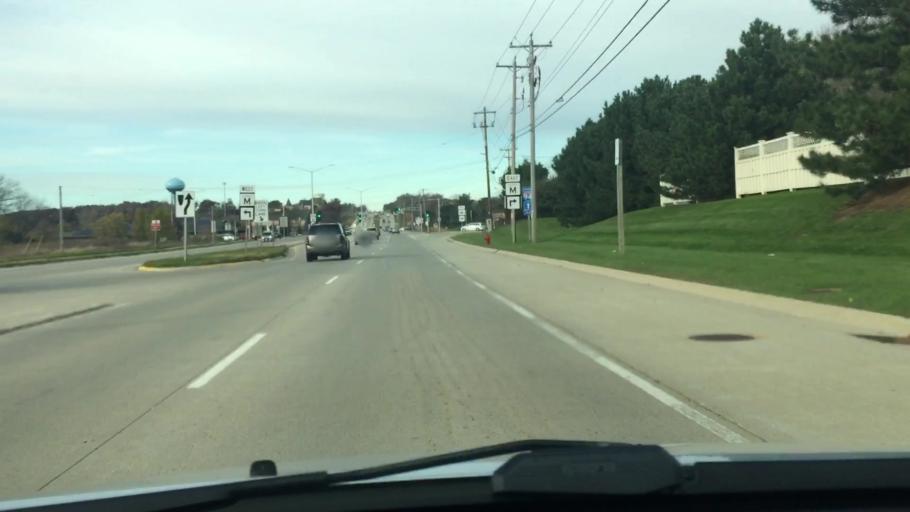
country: US
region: Wisconsin
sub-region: Waukesha County
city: Pewaukee
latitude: 43.0669
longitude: -88.2250
